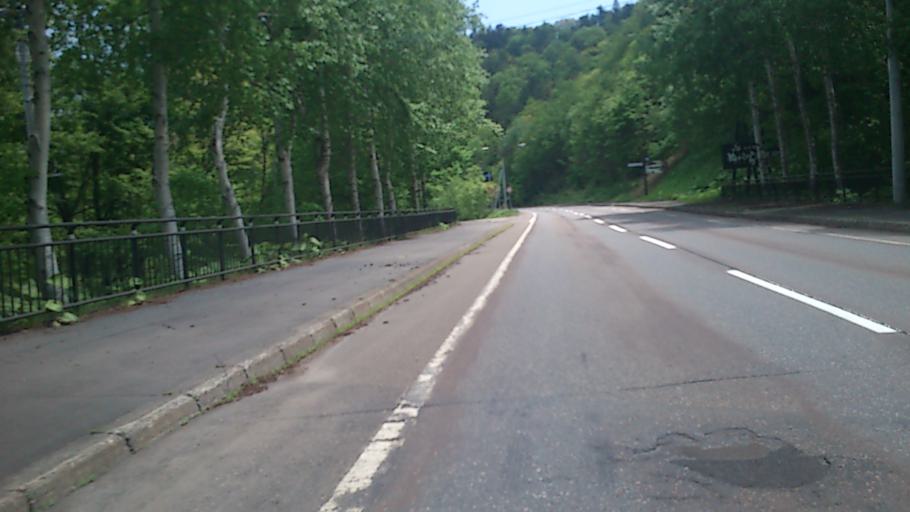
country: JP
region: Hokkaido
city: Otofuke
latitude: 43.3650
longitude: 143.1949
